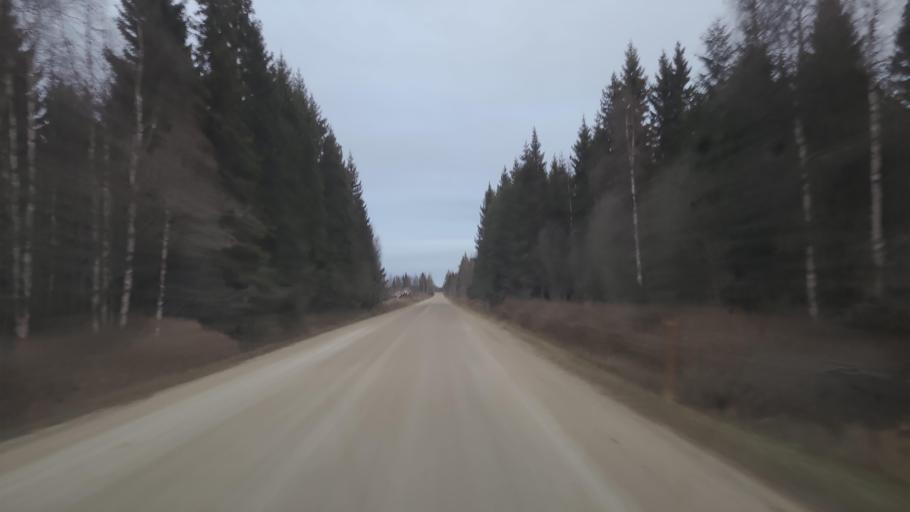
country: FI
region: Lapland
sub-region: Kemi-Tornio
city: Tervola
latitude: 66.0733
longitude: 24.8534
